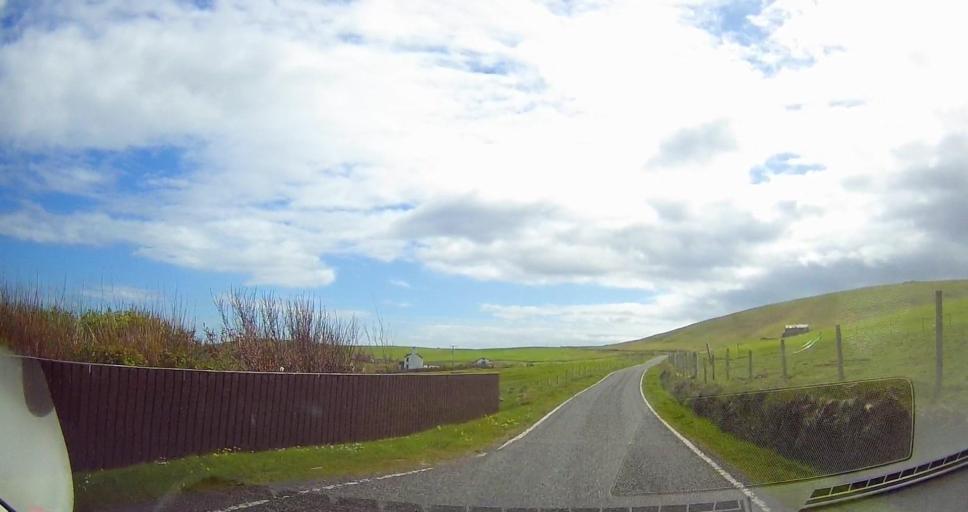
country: GB
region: Scotland
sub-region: Shetland Islands
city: Sandwick
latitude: 59.9309
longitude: -1.3448
